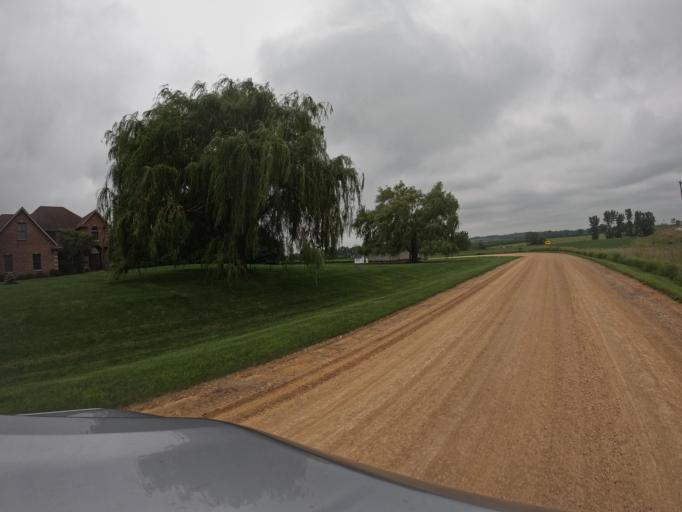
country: US
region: Iowa
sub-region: Clinton County
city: De Witt
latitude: 41.8937
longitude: -90.5895
